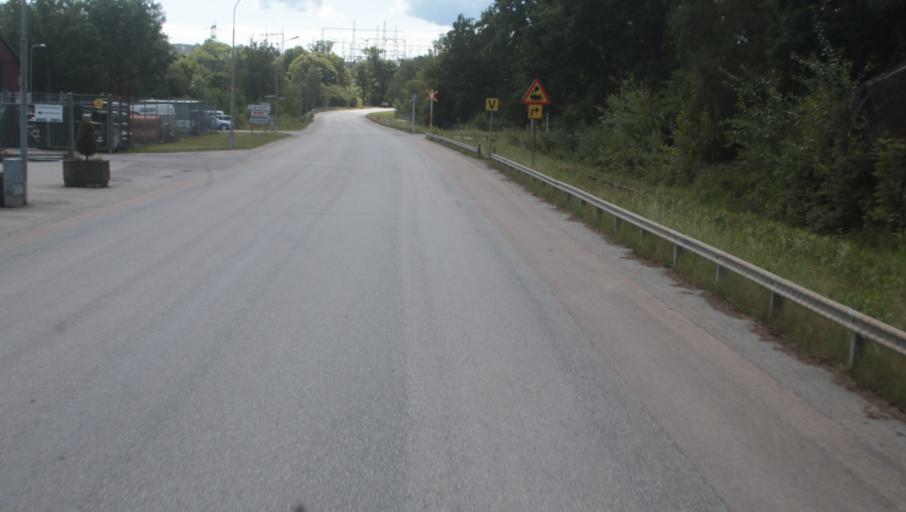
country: SE
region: Blekinge
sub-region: Karlshamns Kommun
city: Karlshamn
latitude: 56.1596
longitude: 14.8420
